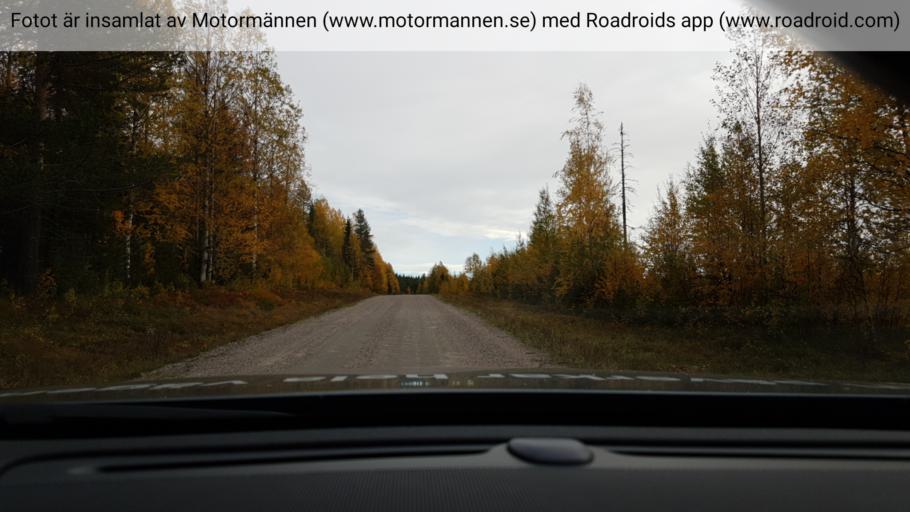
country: SE
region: Norrbotten
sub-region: Overkalix Kommun
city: OEverkalix
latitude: 66.2665
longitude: 23.0132
